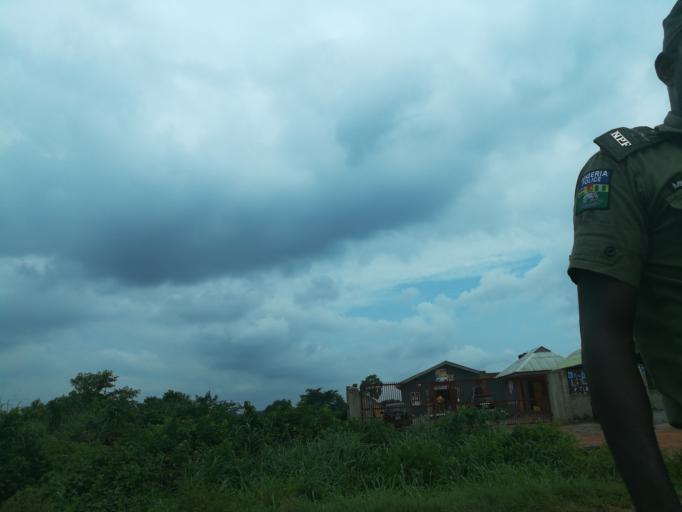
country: NG
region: Lagos
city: Ejirin
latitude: 6.6456
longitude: 3.7290
